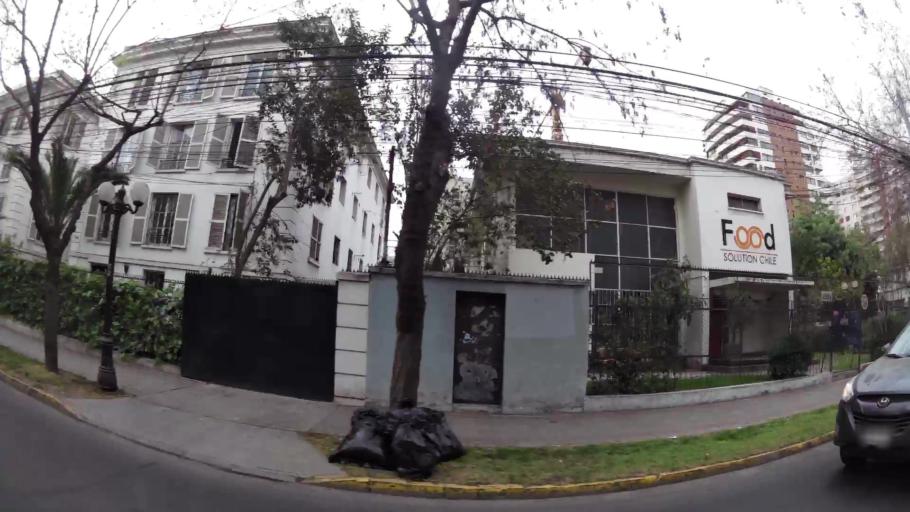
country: CL
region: Santiago Metropolitan
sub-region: Provincia de Santiago
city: Villa Presidente Frei, Nunoa, Santiago, Chile
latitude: -33.4292
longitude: -70.5994
